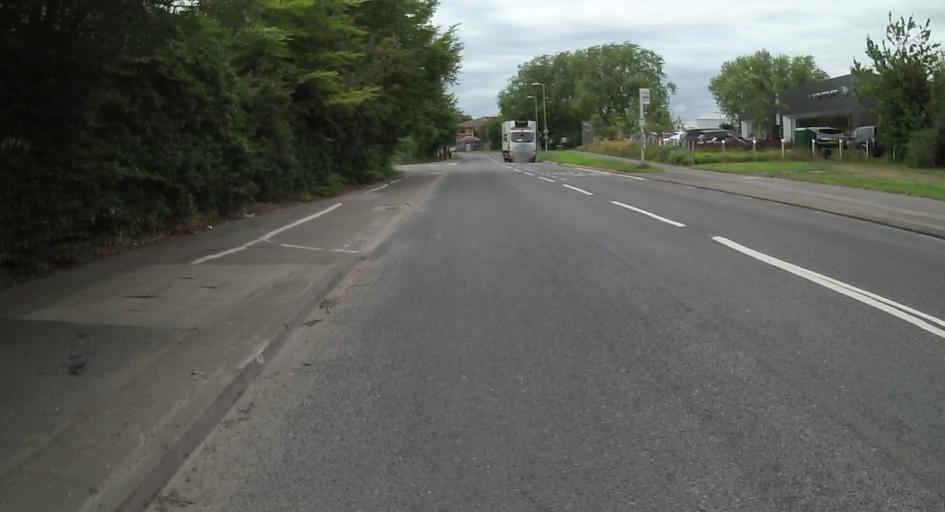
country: GB
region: England
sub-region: Hampshire
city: Basingstoke
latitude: 51.2725
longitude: -1.1004
